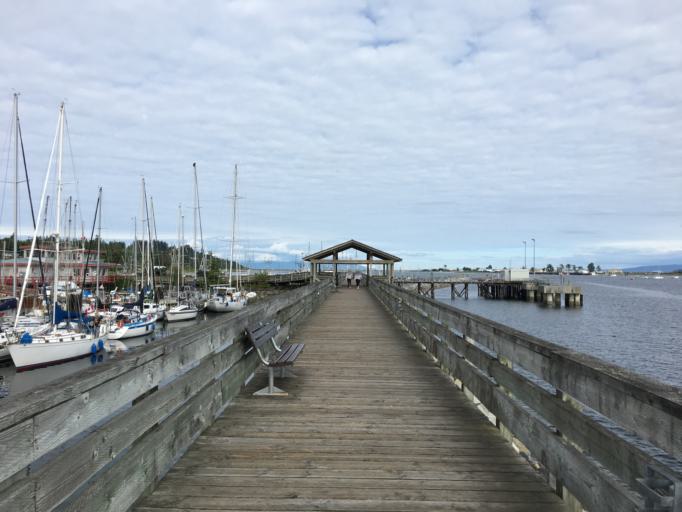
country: CA
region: British Columbia
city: Courtenay
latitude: 49.6693
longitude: -124.9291
